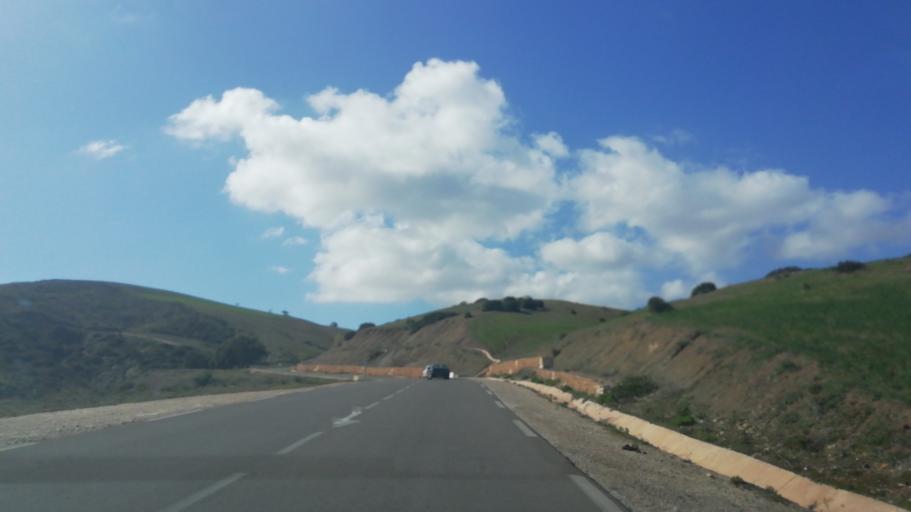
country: DZ
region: Relizane
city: Relizane
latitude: 36.0814
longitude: 0.4841
